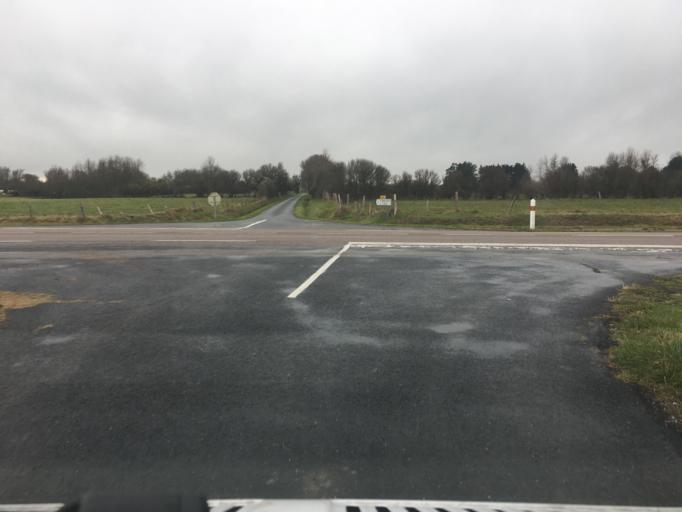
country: FR
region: Lower Normandy
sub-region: Departement de la Manche
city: Sainte-Mere-Eglise
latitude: 49.4795
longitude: -1.2564
